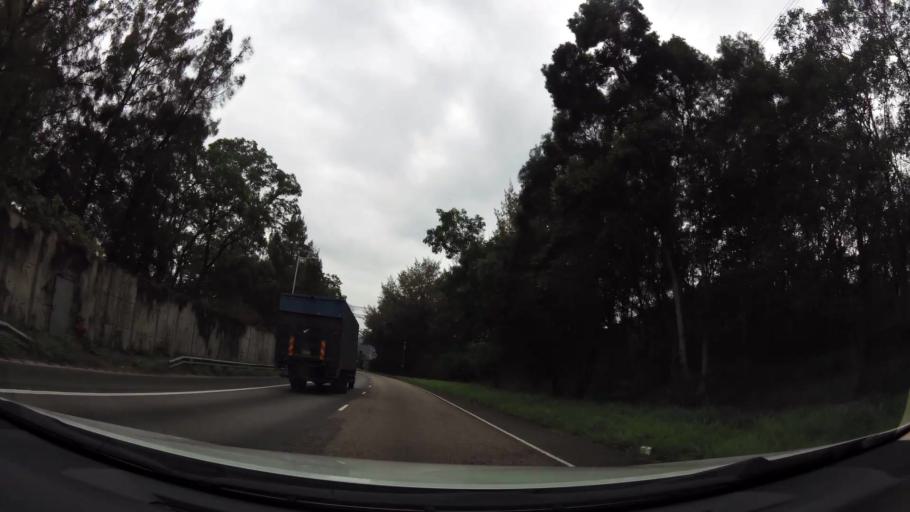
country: HK
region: Yuen Long
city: Yuen Long Kau Hui
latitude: 22.4445
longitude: 114.0507
